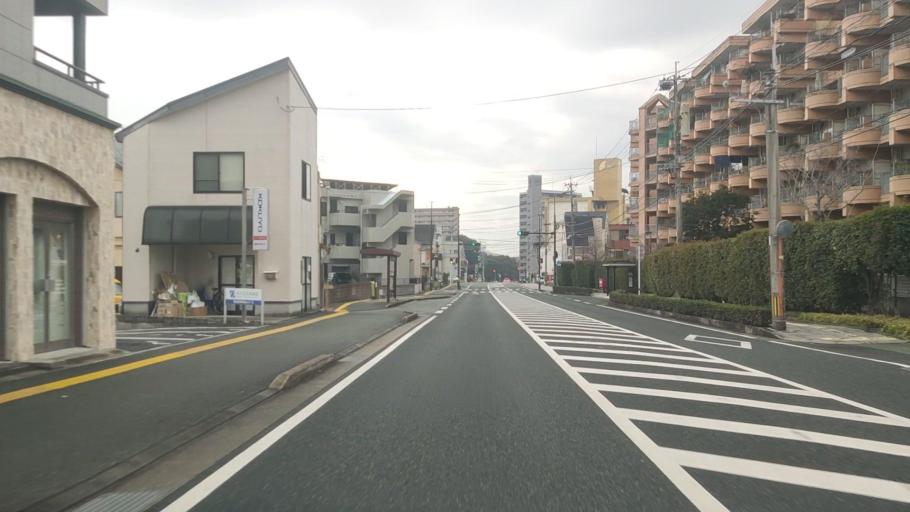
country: JP
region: Kumamoto
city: Kumamoto
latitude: 32.7902
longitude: 130.7395
